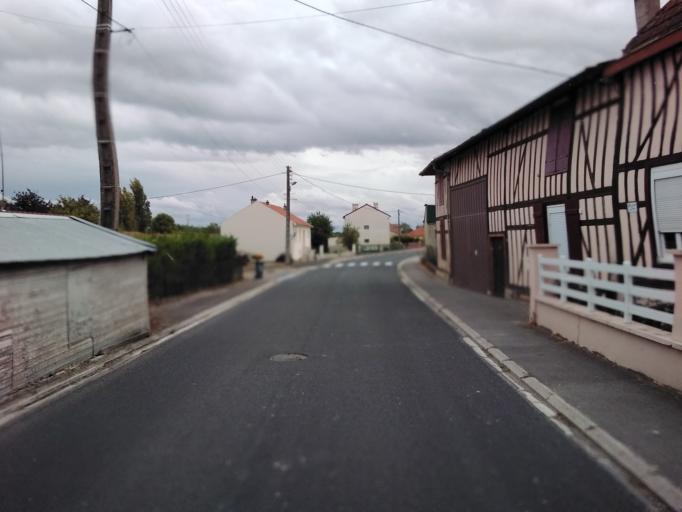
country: FR
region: Champagne-Ardenne
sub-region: Departement de la Marne
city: Frignicourt
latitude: 48.6713
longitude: 4.5835
